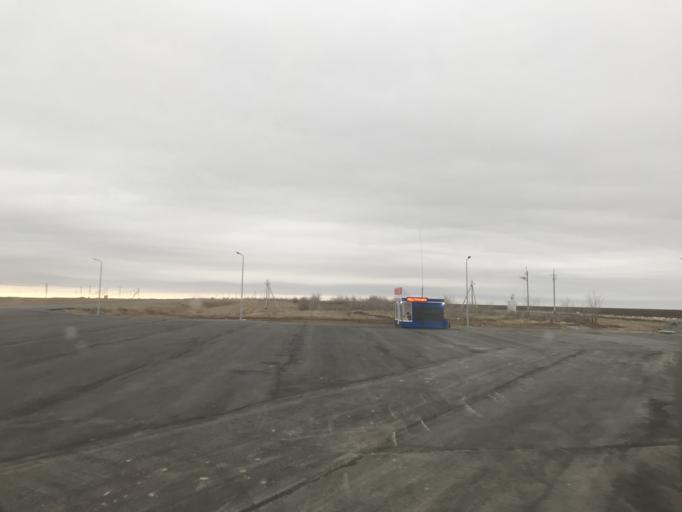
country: KZ
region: Batys Qazaqstan
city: Peremetnoe
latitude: 51.6470
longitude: 51.0117
